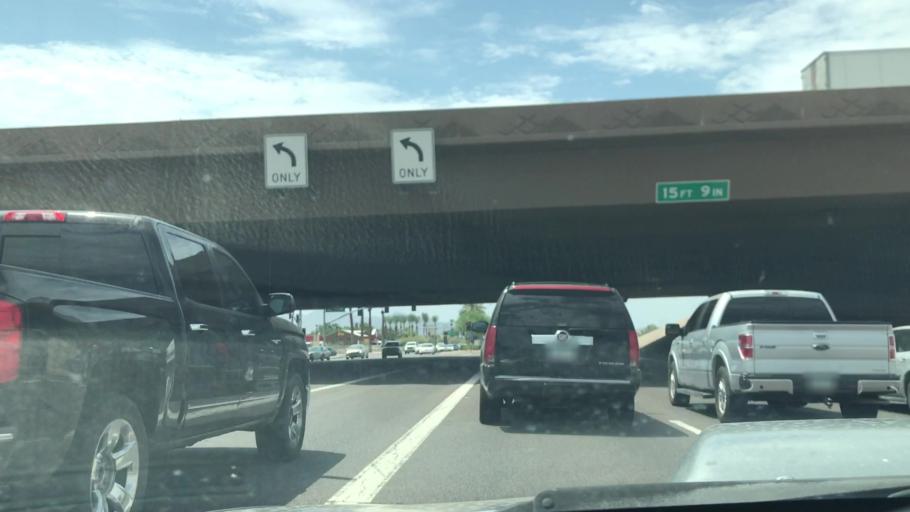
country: US
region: Arizona
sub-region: Maricopa County
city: Goodyear
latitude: 33.4584
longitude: -112.3582
